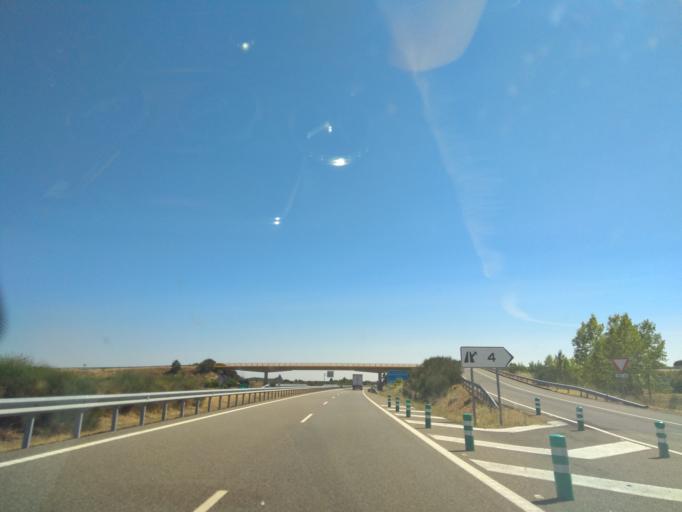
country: ES
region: Castille and Leon
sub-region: Provincia de Leon
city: Vega de Infanzones
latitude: 42.4862
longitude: -5.5550
